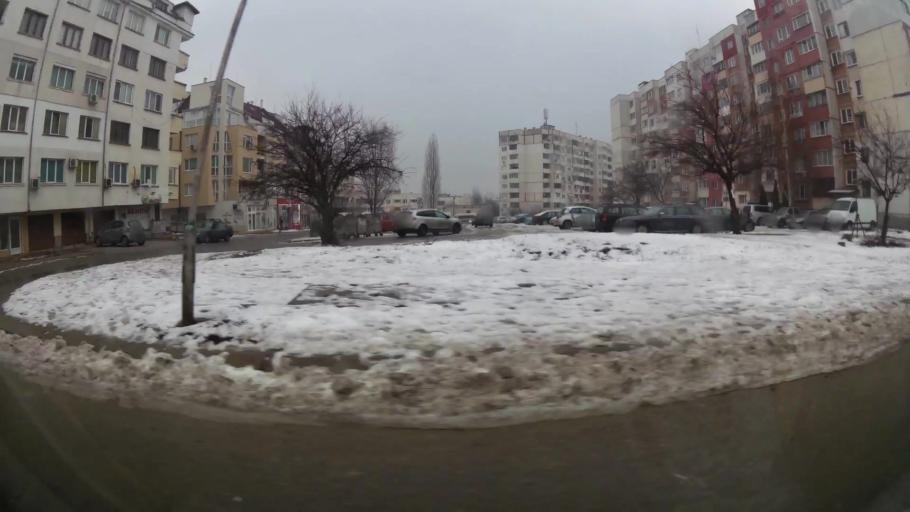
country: BG
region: Sofia-Capital
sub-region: Stolichna Obshtina
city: Sofia
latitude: 42.6850
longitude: 23.2506
